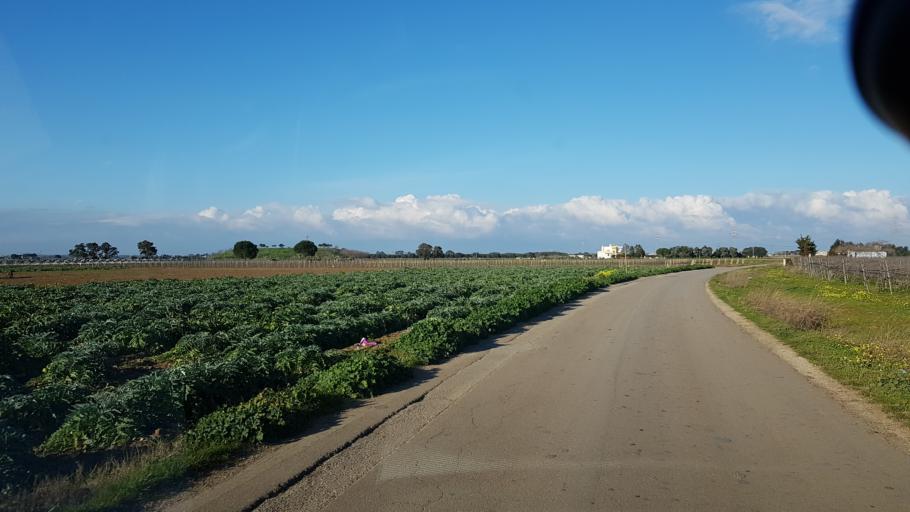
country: IT
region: Apulia
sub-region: Provincia di Brindisi
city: Tuturano
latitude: 40.5747
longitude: 17.8999
